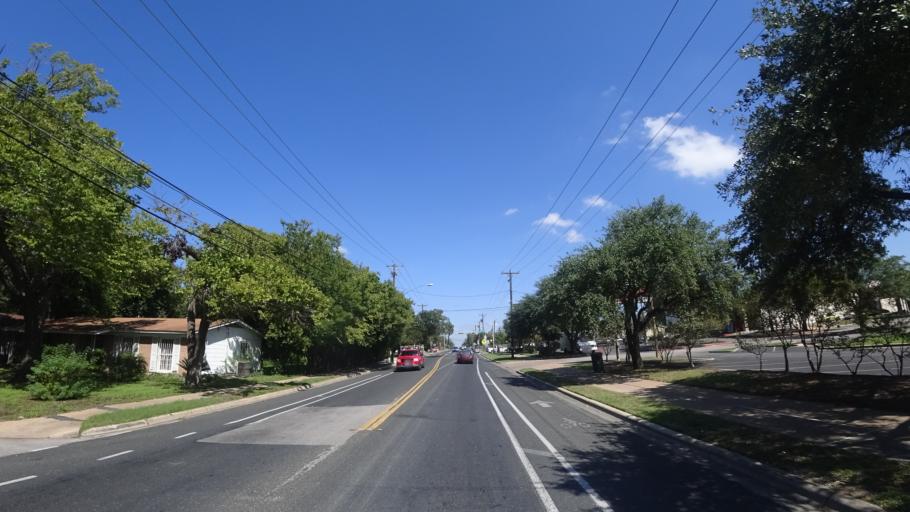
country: US
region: Texas
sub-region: Travis County
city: Austin
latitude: 30.3134
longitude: -97.6930
